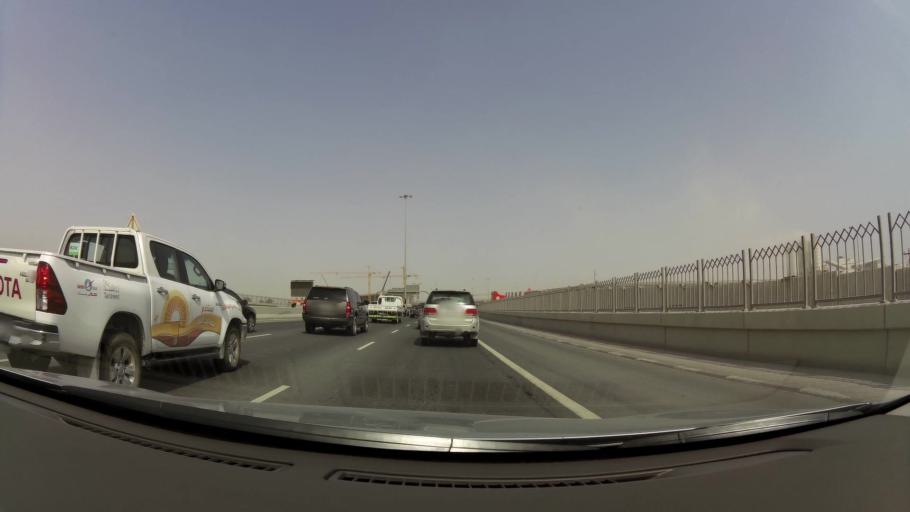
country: QA
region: Baladiyat ad Dawhah
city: Doha
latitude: 25.2914
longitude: 51.4769
